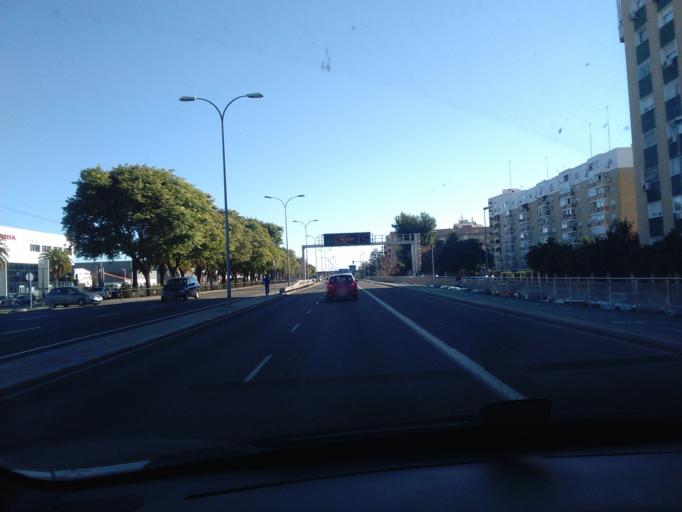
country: ES
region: Andalusia
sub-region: Provincia de Sevilla
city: Sevilla
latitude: 37.3866
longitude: -5.9463
